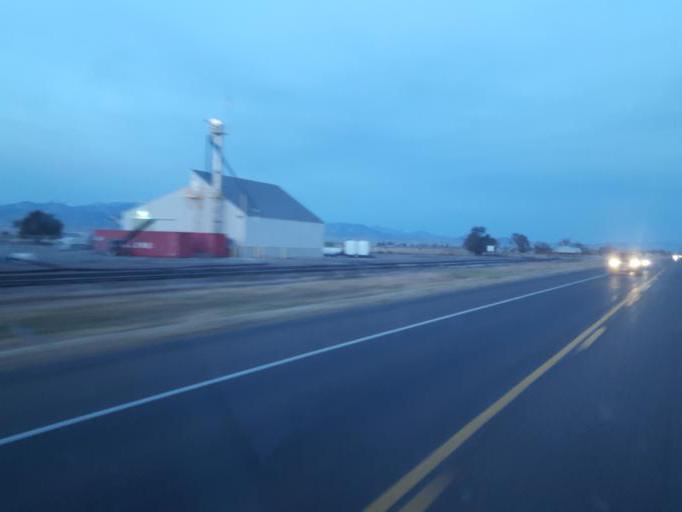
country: US
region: Colorado
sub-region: Rio Grande County
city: Monte Vista
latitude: 37.5617
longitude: -106.0990
